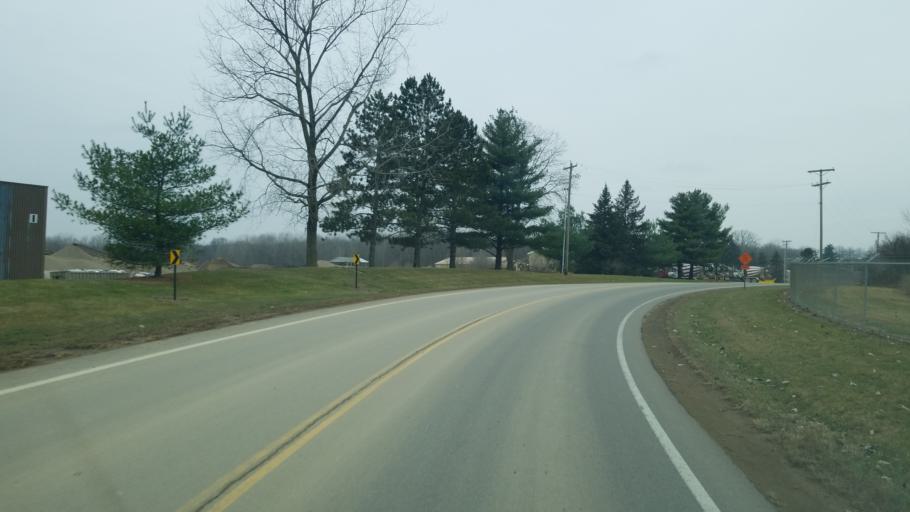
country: US
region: Ohio
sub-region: Knox County
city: Mount Vernon
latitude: 40.3757
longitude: -82.4930
